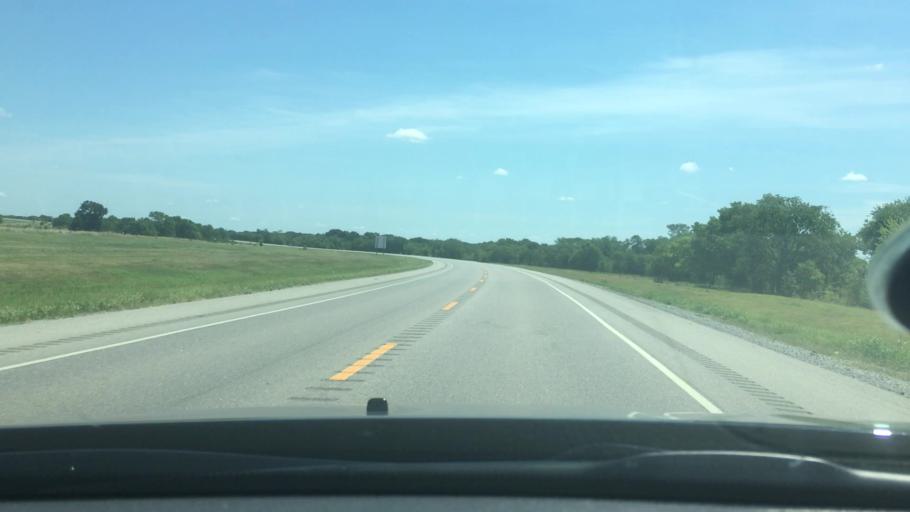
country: US
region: Oklahoma
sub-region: Bryan County
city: Durant
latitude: 33.9653
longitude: -96.3534
